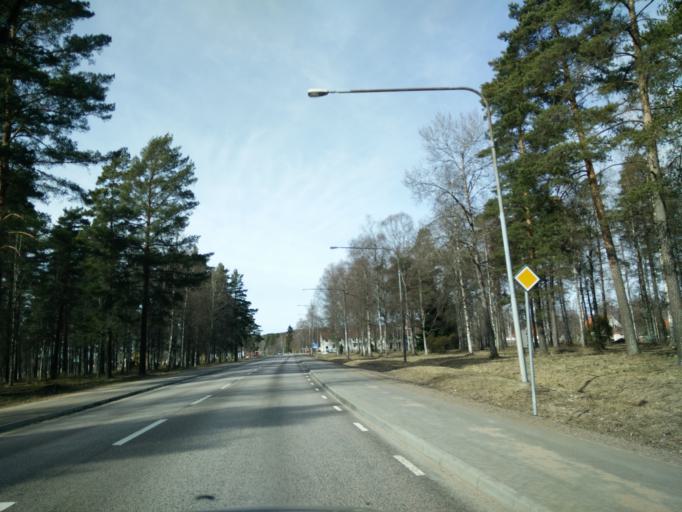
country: SE
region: Vaermland
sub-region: Hagfors Kommun
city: Hagfors
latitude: 60.0216
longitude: 13.6213
